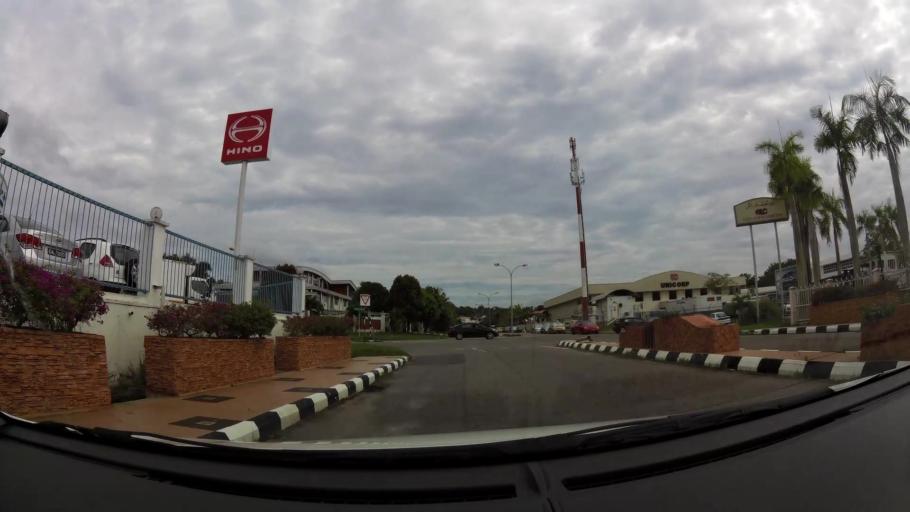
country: BN
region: Brunei and Muara
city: Bandar Seri Begawan
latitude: 4.8932
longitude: 114.9050
